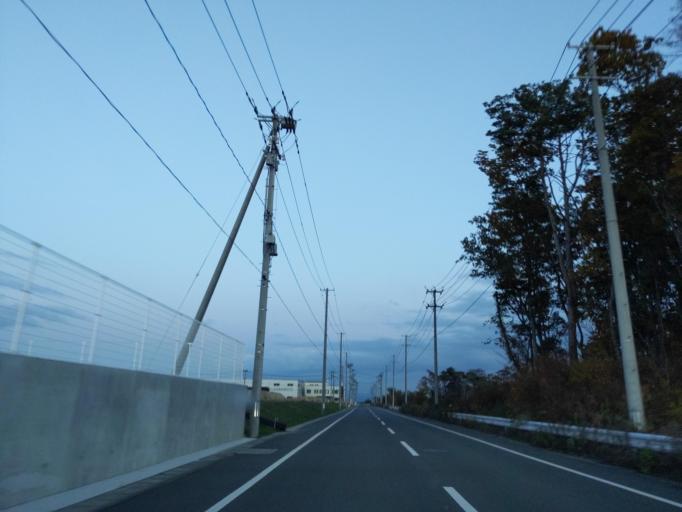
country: JP
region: Fukushima
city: Koriyama
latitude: 37.4585
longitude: 140.2990
